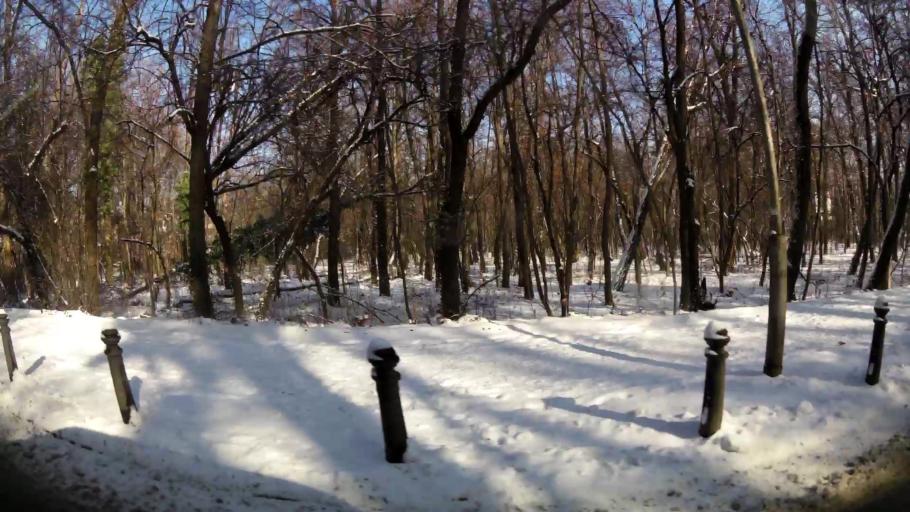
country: BG
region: Sofia-Capital
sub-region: Stolichna Obshtina
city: Sofia
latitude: 42.6655
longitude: 23.3160
